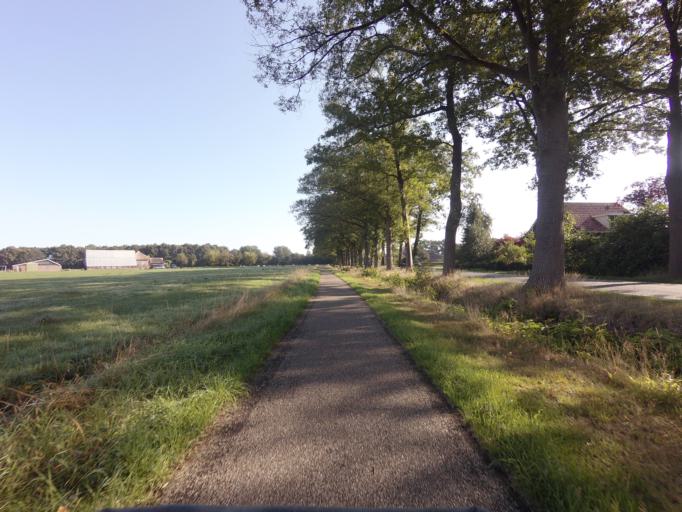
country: NL
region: Overijssel
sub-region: Gemeente Deventer
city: Schalkhaar
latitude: 52.2984
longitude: 6.2633
